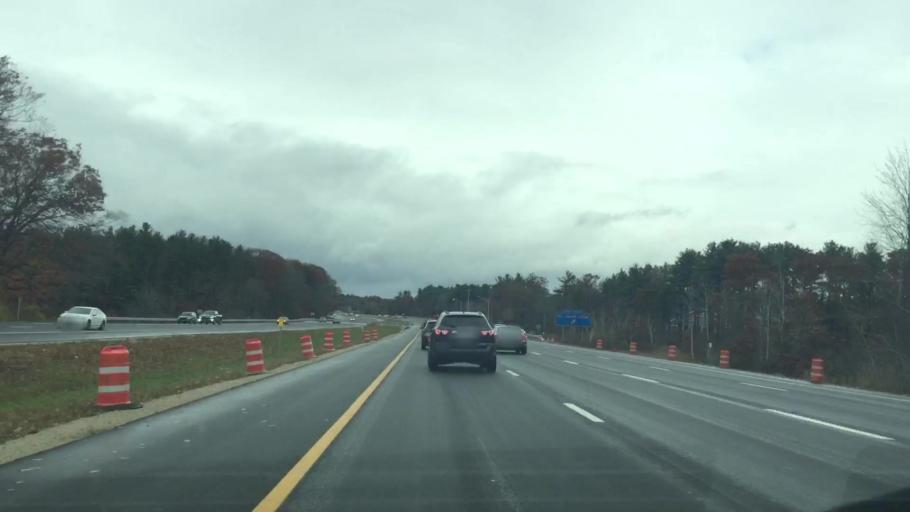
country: US
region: New Hampshire
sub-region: Rockingham County
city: Hampton Falls
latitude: 42.9311
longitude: -70.8640
